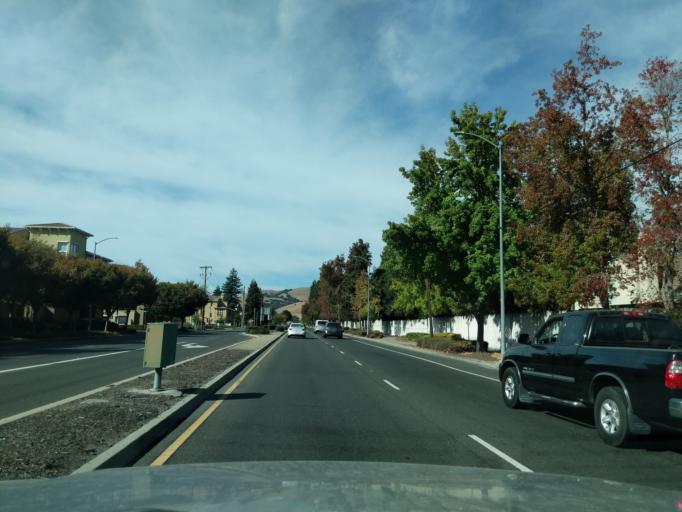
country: US
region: California
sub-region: Alameda County
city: Fremont
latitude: 37.5658
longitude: -121.9618
